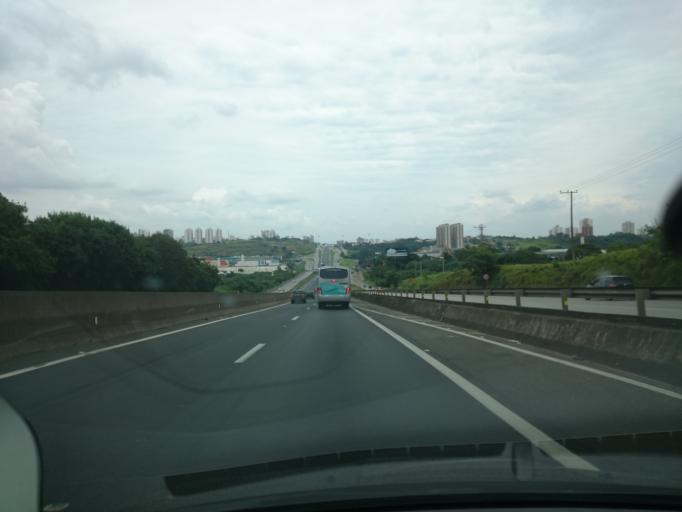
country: BR
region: Sao Paulo
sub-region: Votorantim
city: Votorantim
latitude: -23.5252
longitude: -47.4425
